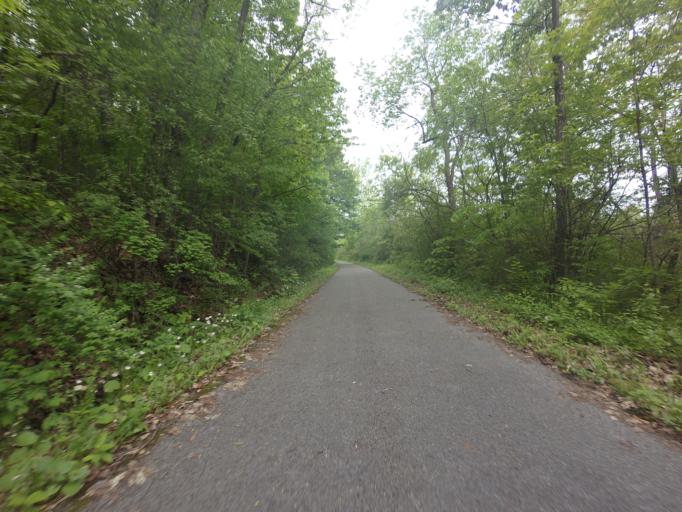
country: US
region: New York
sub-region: Jefferson County
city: Calcium
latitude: 43.9838
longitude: -75.8489
